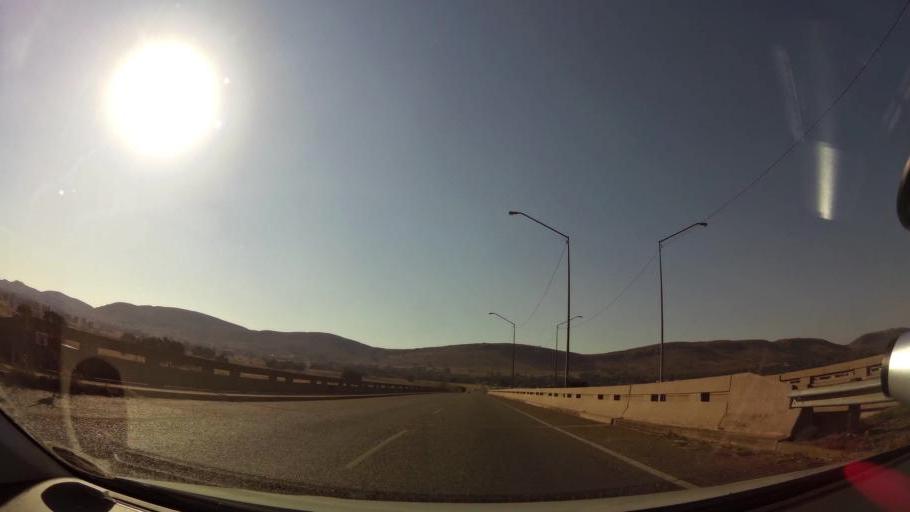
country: ZA
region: Gauteng
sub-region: City of Tshwane Metropolitan Municipality
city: Pretoria
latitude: -25.7046
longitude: 28.1379
